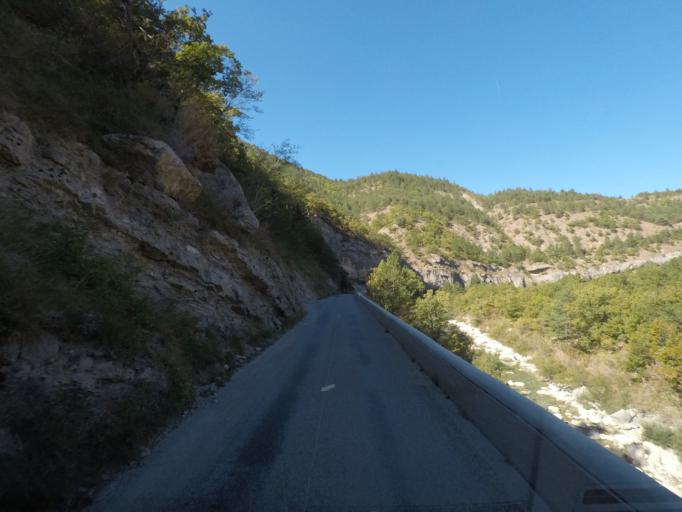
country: FR
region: Rhone-Alpes
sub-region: Departement de la Drome
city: Die
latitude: 44.6534
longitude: 5.2855
